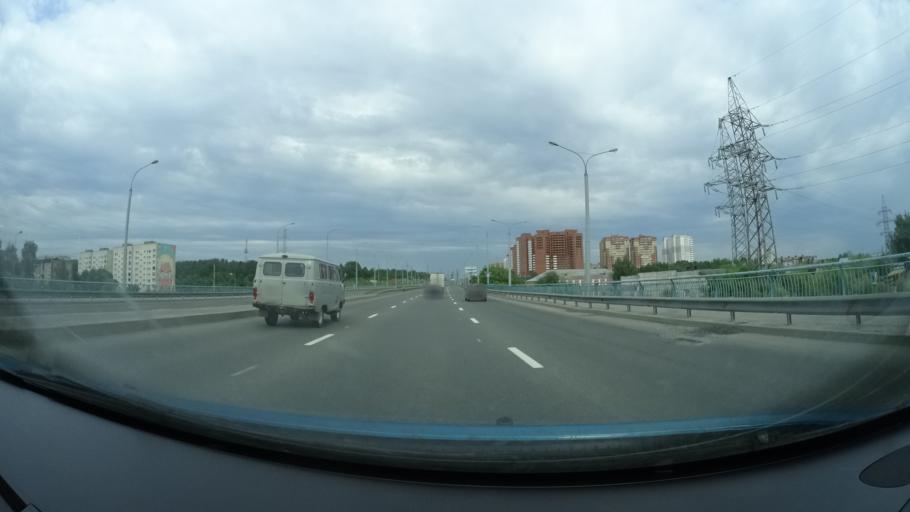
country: RU
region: Perm
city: Perm
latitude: 57.9861
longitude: 56.2719
